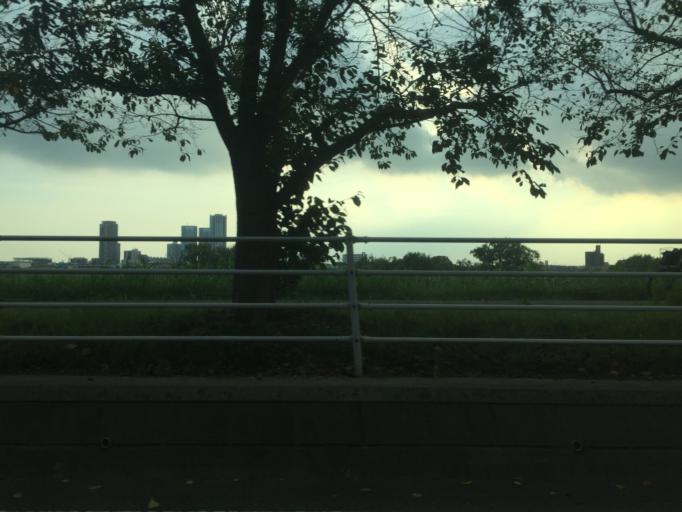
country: JP
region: Kanagawa
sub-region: Kawasaki-shi
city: Kawasaki
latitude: 35.5635
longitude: 139.6829
